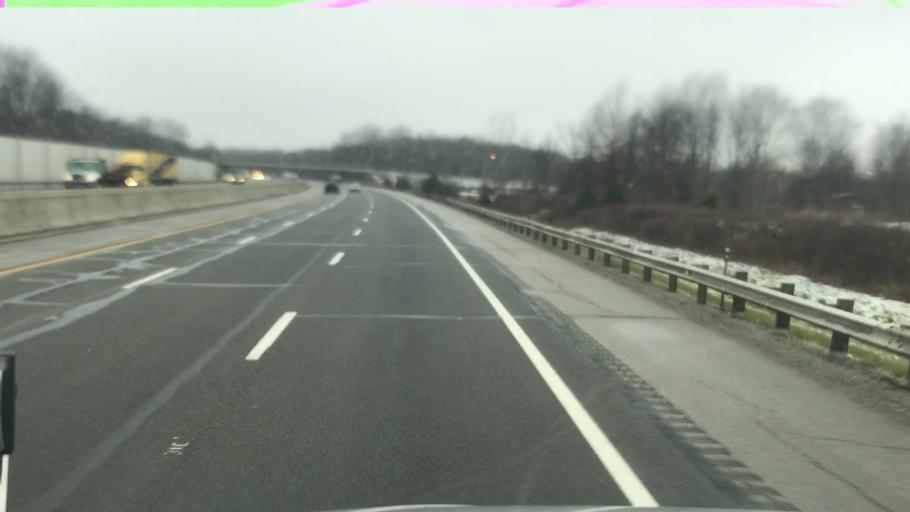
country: US
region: Ohio
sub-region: Cuyahoga County
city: Olmsted Falls
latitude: 41.3691
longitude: -81.9400
